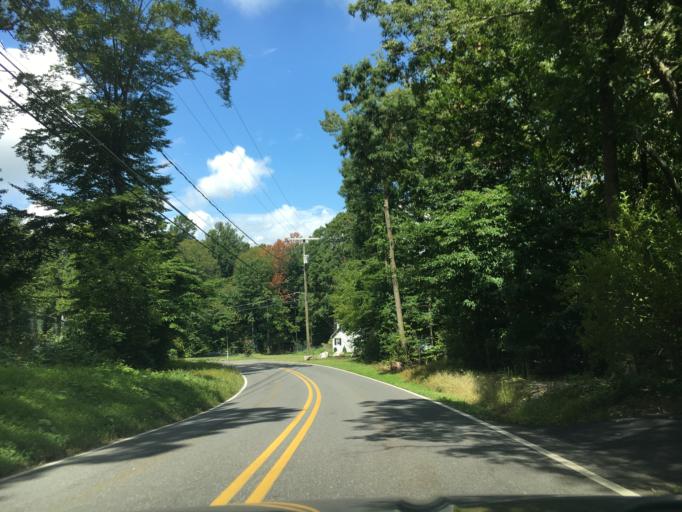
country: US
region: Pennsylvania
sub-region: Berks County
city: Fleetwood
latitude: 40.4461
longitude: -75.8032
